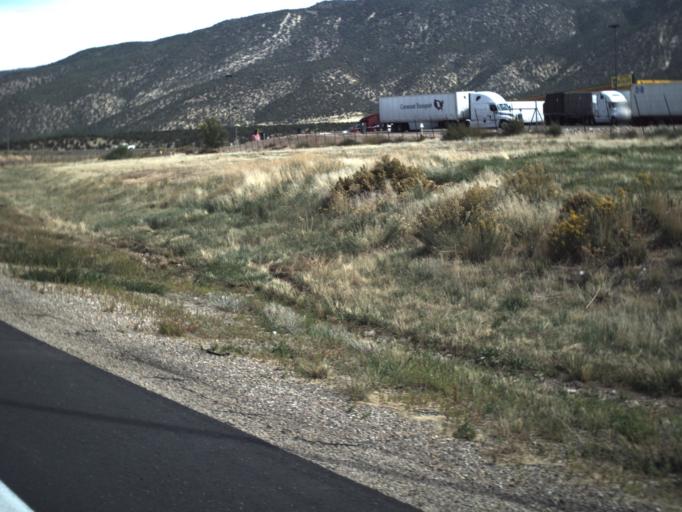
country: US
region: Utah
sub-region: Iron County
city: Cedar City
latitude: 37.7262
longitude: -113.0537
